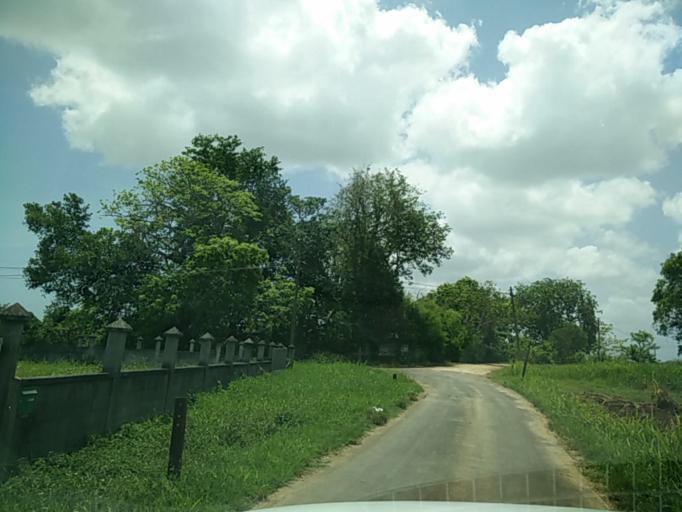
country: GP
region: Guadeloupe
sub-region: Guadeloupe
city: Les Abymes
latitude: 16.2878
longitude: -61.5228
